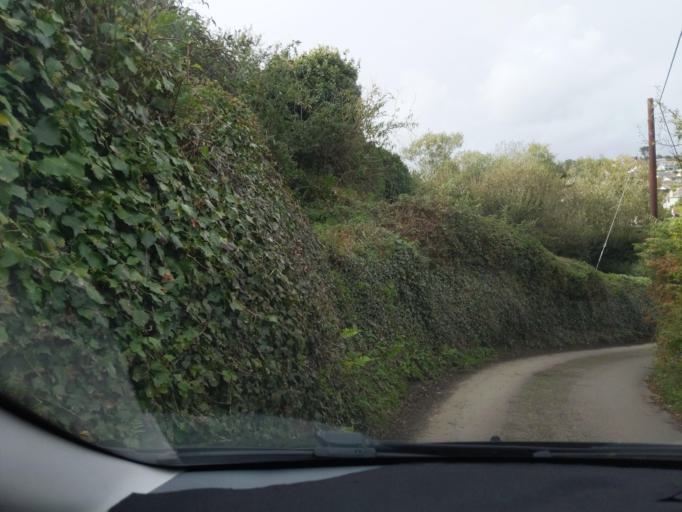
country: GB
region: England
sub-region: Cornwall
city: Mevagissey
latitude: 50.2385
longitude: -4.7903
